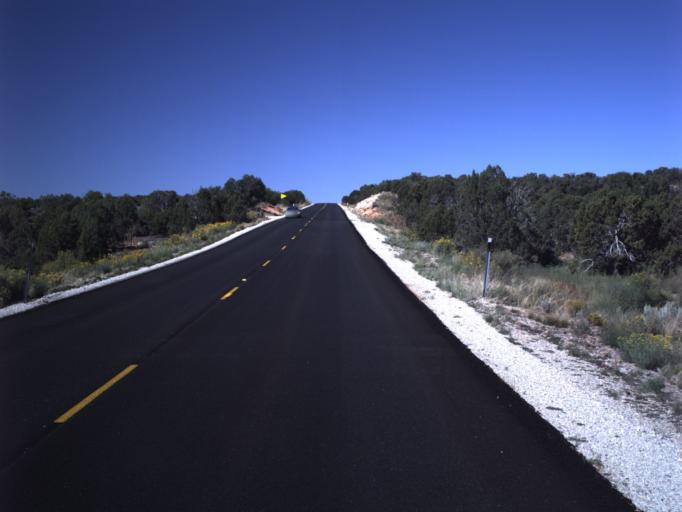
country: US
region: Utah
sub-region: San Juan County
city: Blanding
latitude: 37.5768
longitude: -109.5232
